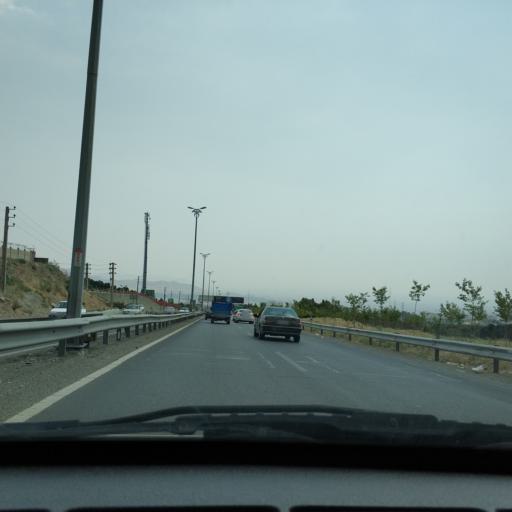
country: IR
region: Tehran
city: Tajrish
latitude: 35.7797
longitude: 51.5625
